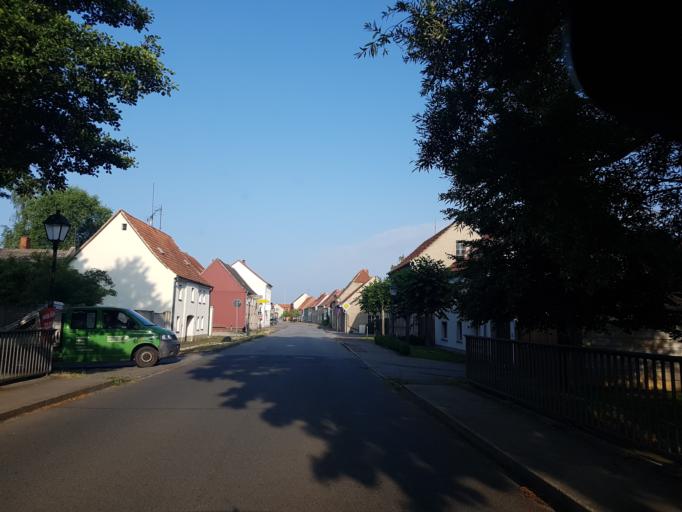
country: DE
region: Saxony-Anhalt
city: Holzdorf
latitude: 51.8143
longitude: 13.2334
